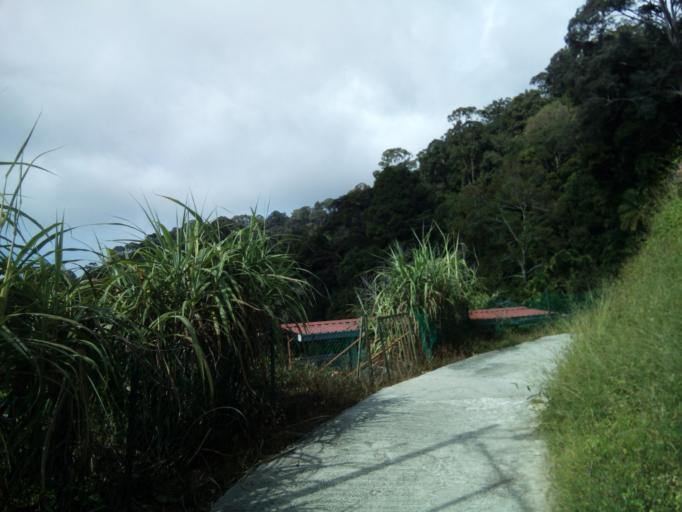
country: MY
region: Penang
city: Tanjung Tokong
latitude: 5.4167
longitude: 100.2674
